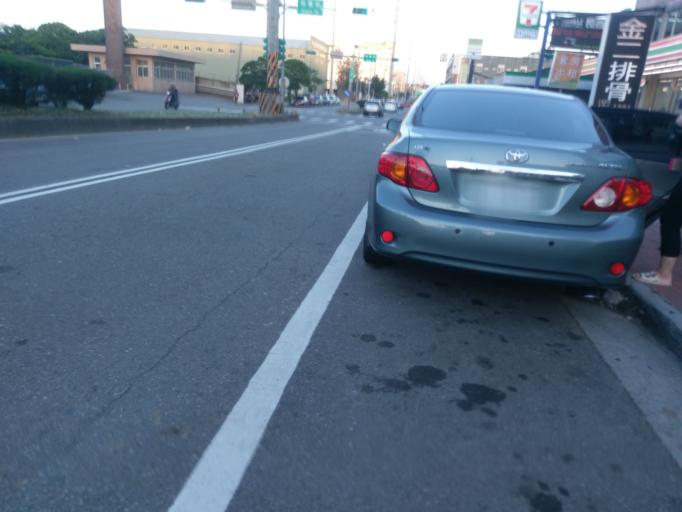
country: TW
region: Taiwan
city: Taoyuan City
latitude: 25.0548
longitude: 121.1238
